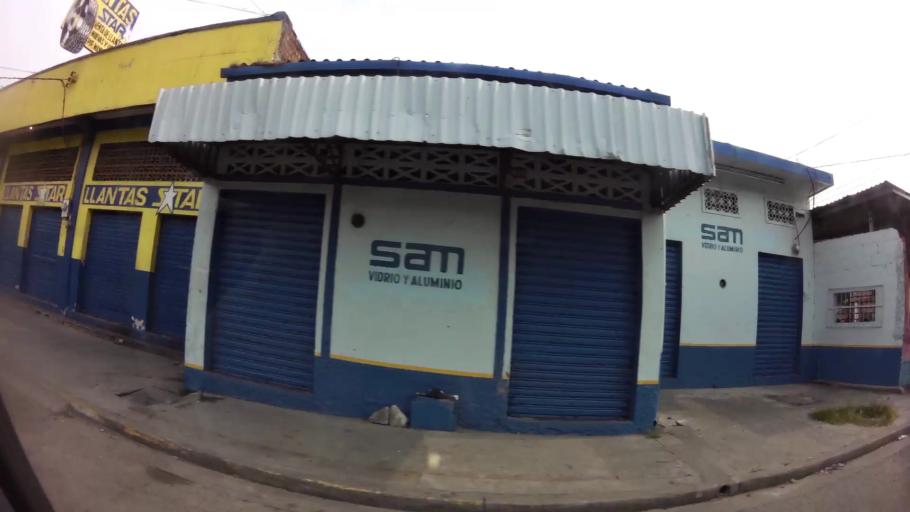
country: HN
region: Cortes
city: San Pedro Sula
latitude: 15.4944
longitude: -88.0233
